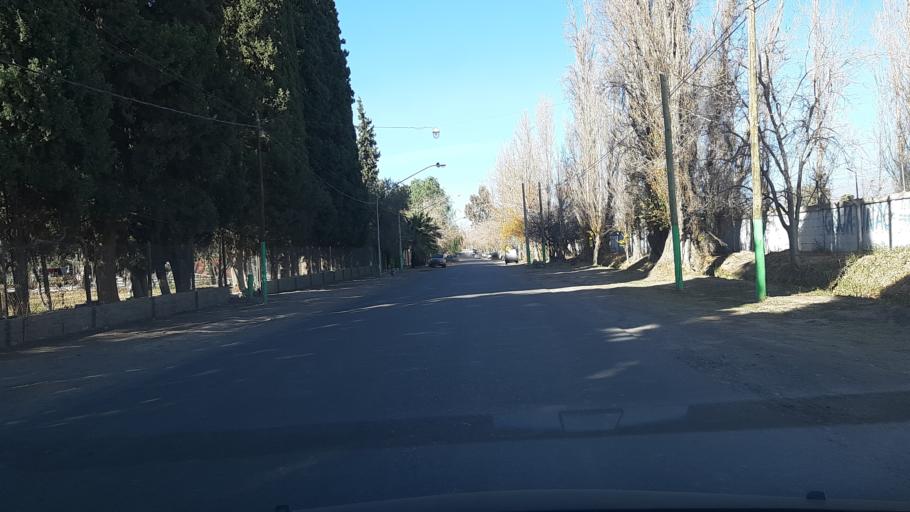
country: AR
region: San Juan
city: San Juan
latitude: -31.5268
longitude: -68.5919
